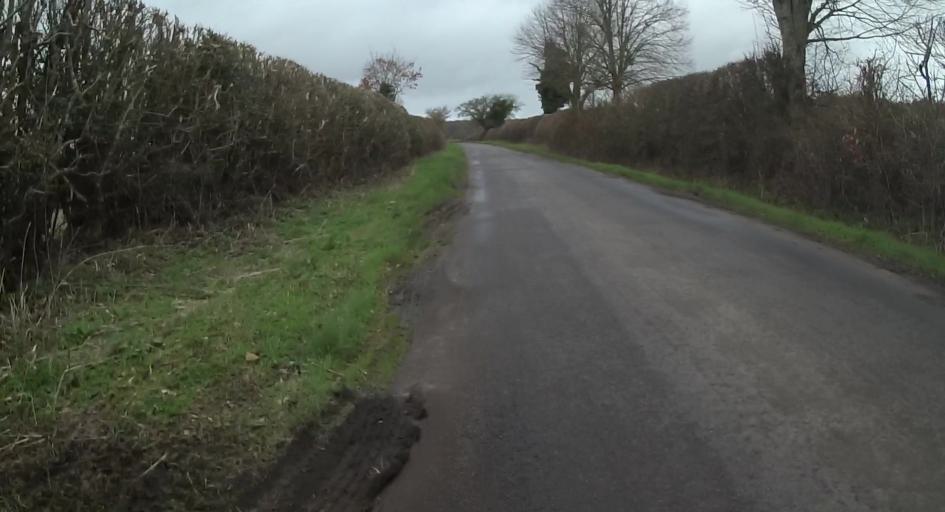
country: GB
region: England
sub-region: Hampshire
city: Overton
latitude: 51.2692
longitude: -1.1980
